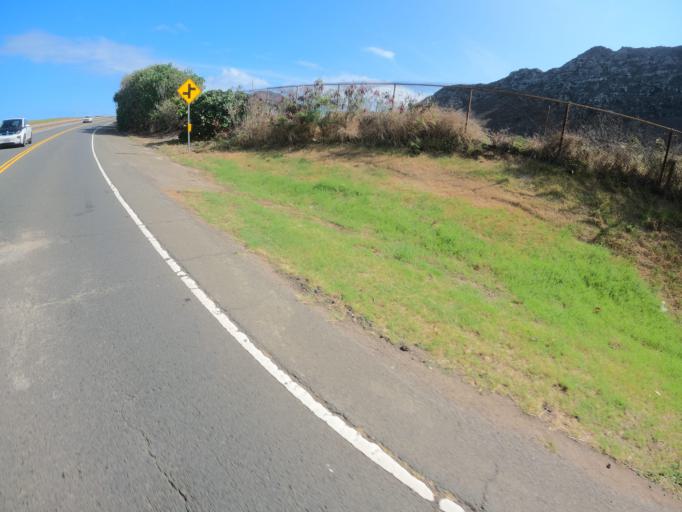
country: US
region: Hawaii
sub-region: Honolulu County
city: Waimanalo Beach
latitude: 21.3155
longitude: -157.6651
